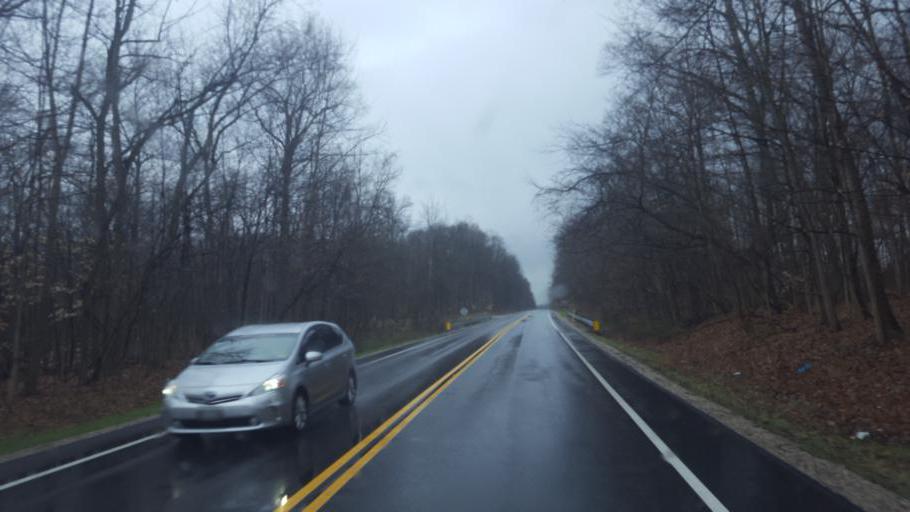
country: US
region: Ohio
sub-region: Delaware County
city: Lewis Center
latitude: 40.1955
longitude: -82.9788
